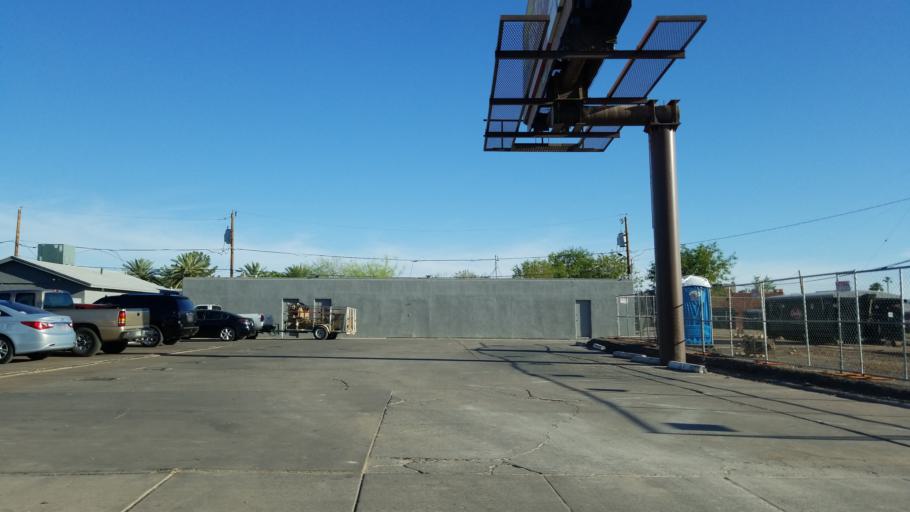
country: US
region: Arizona
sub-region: Maricopa County
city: Phoenix
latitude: 33.4512
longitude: -112.0194
